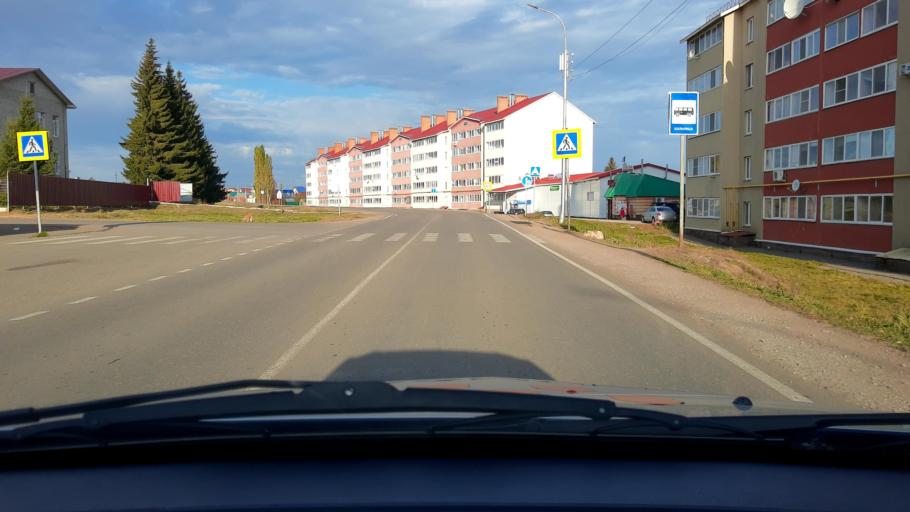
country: RU
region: Bashkortostan
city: Mikhaylovka
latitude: 54.8154
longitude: 55.7987
